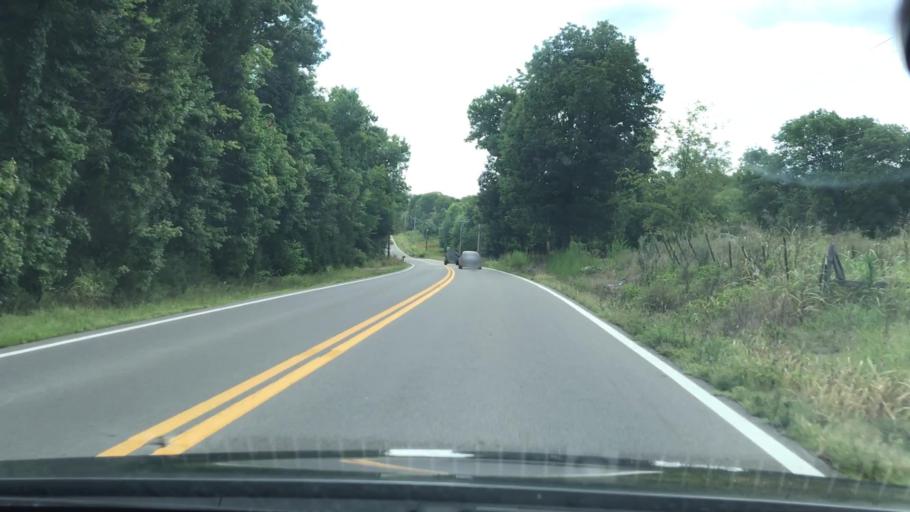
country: US
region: Tennessee
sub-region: Williamson County
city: Nolensville
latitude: 35.8509
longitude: -86.5974
